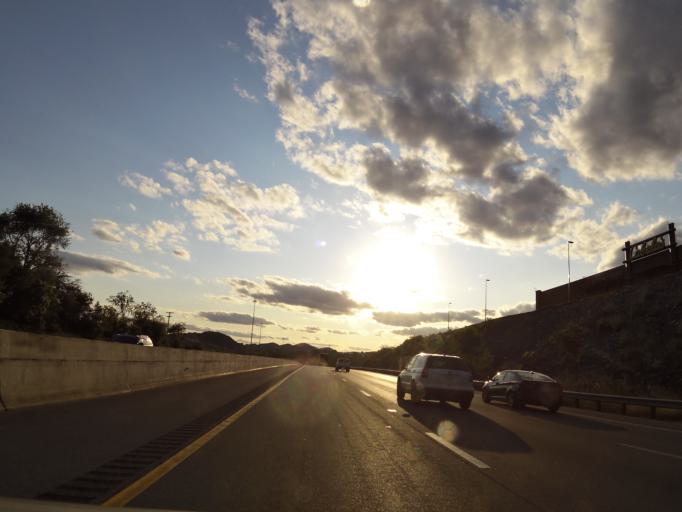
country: US
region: Tennessee
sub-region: Sullivan County
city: Fairmount
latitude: 36.6255
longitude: -82.1466
